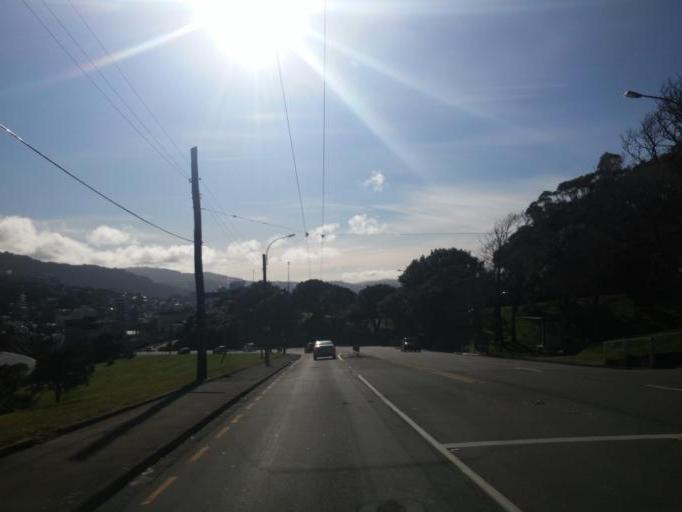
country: NZ
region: Wellington
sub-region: Wellington City
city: Wellington
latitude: -41.3032
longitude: 174.7693
